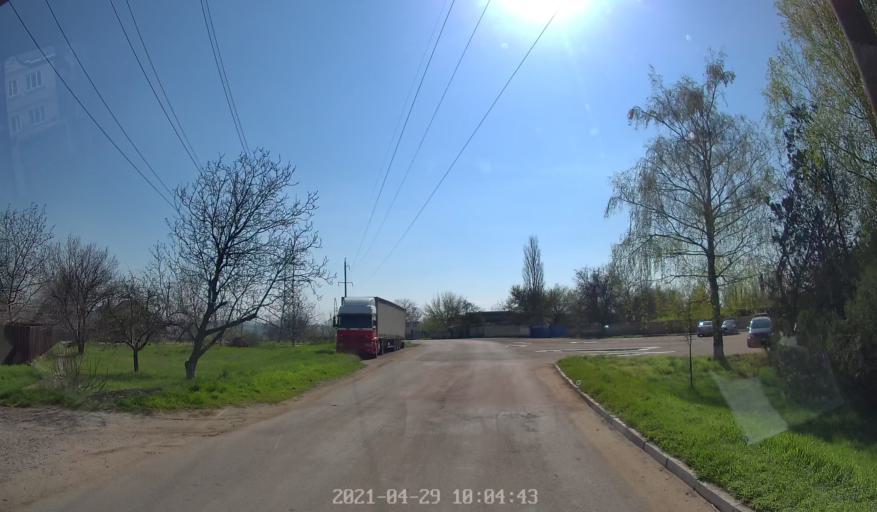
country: MD
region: Chisinau
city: Cricova
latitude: 47.1460
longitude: 28.8565
